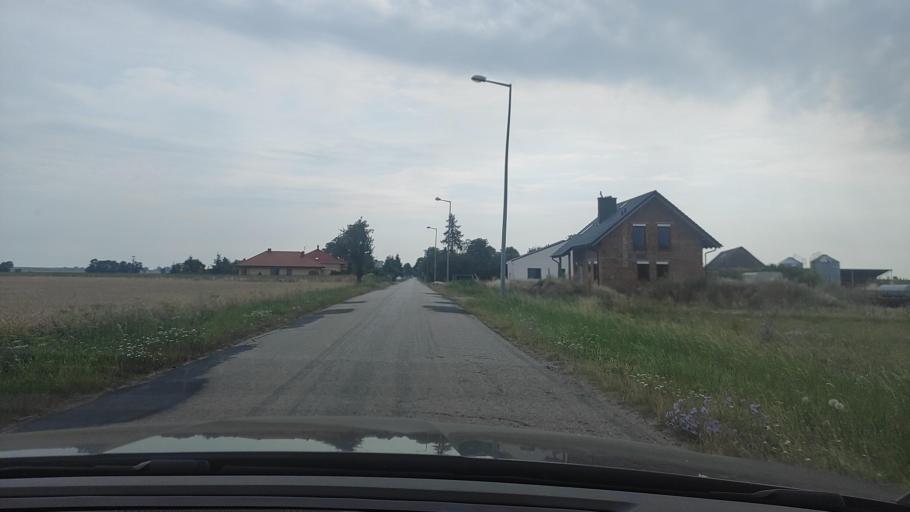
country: PL
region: Greater Poland Voivodeship
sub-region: Powiat poznanski
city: Kleszczewo
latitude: 52.2973
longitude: 17.1345
